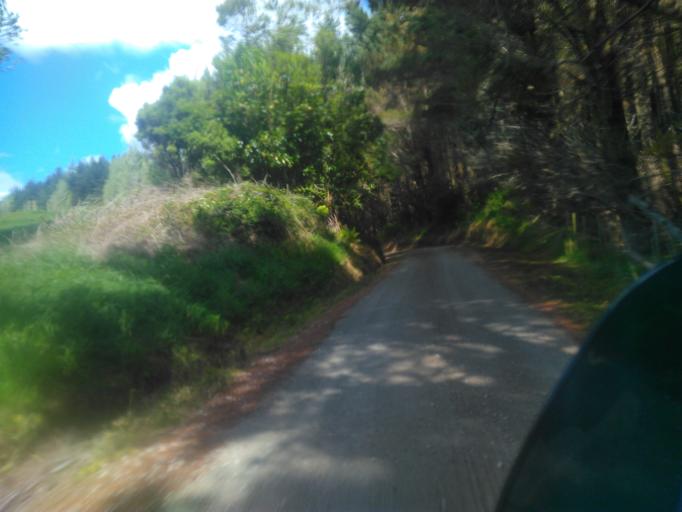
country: NZ
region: Hawke's Bay
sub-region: Wairoa District
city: Wairoa
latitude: -38.7704
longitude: 177.5974
